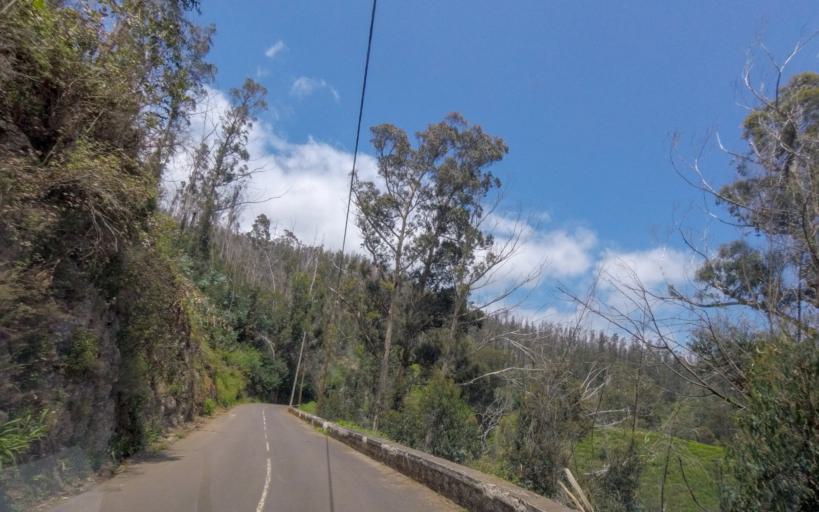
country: PT
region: Madeira
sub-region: Funchal
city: Nossa Senhora do Monte
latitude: 32.6810
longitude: -16.8880
